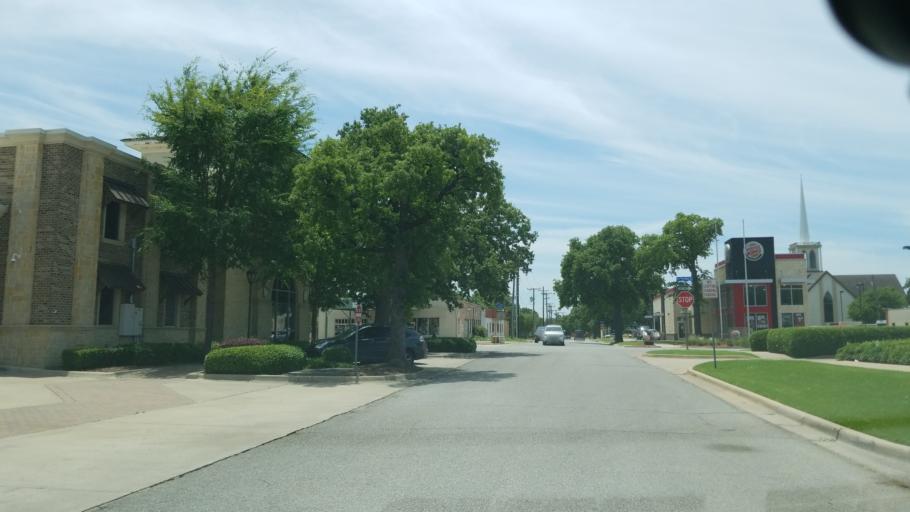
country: US
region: Texas
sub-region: Dallas County
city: Irving
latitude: 32.8143
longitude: -96.9475
